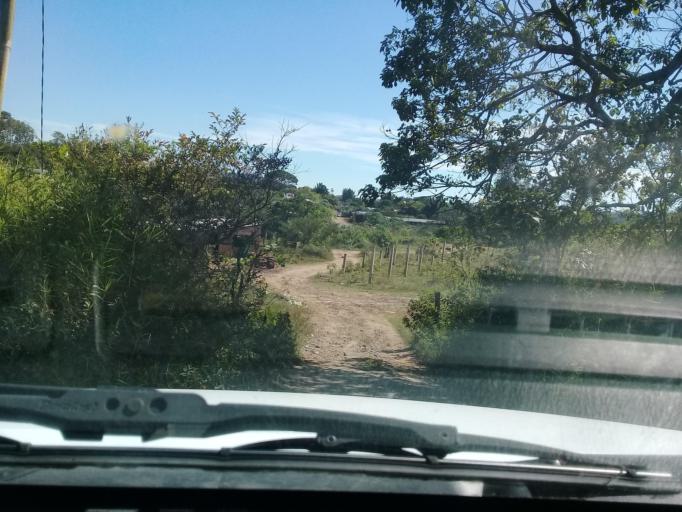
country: MX
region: Veracruz
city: El Castillo
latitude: 19.5513
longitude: -96.8558
